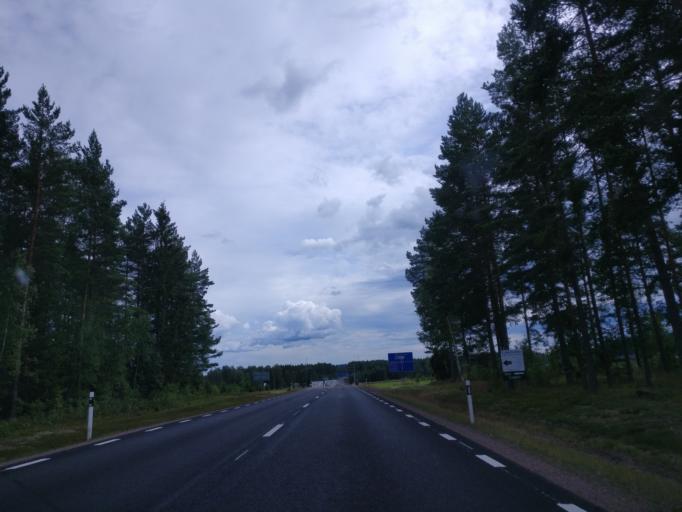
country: SE
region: Vaermland
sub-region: Hagfors Kommun
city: Hagfors
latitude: 60.0385
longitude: 13.5863
